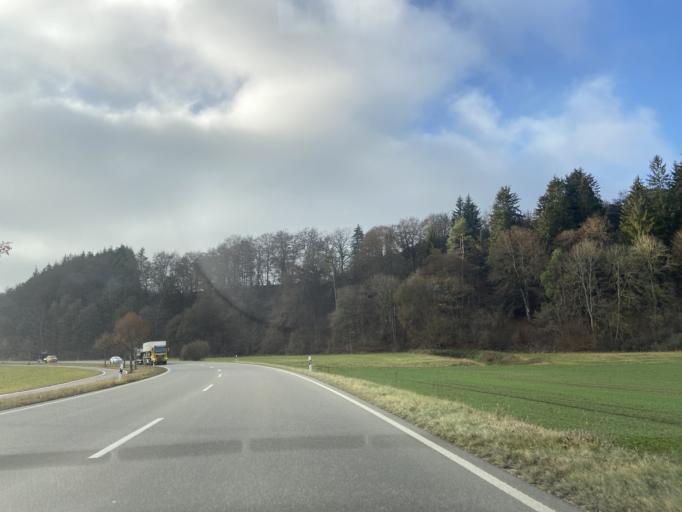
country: DE
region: Baden-Wuerttemberg
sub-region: Tuebingen Region
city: Gammertingen
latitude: 48.2681
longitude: 9.2139
